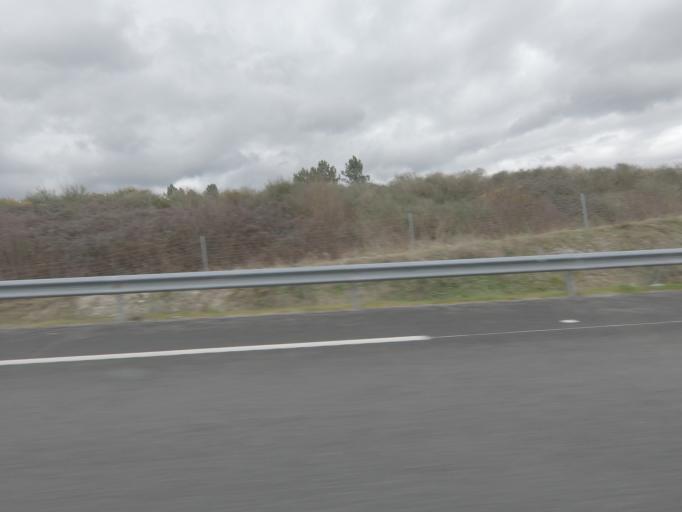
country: ES
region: Galicia
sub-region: Provincia de Ourense
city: Maside
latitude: 42.4135
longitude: -8.0139
